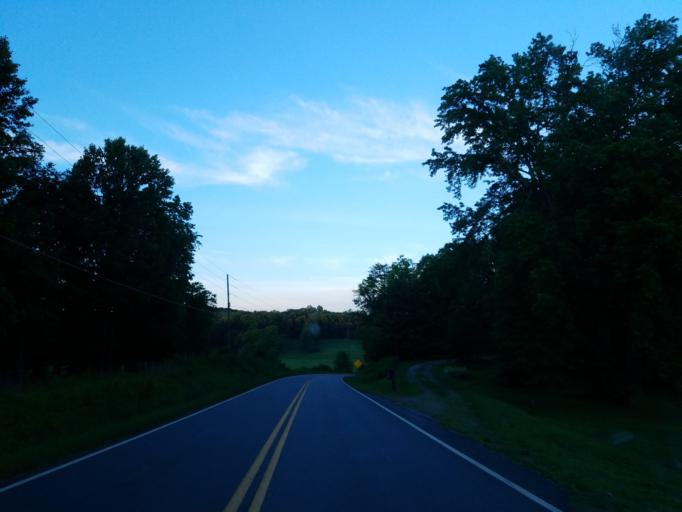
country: US
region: Georgia
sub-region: Lumpkin County
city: Dahlonega
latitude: 34.5660
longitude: -83.9627
